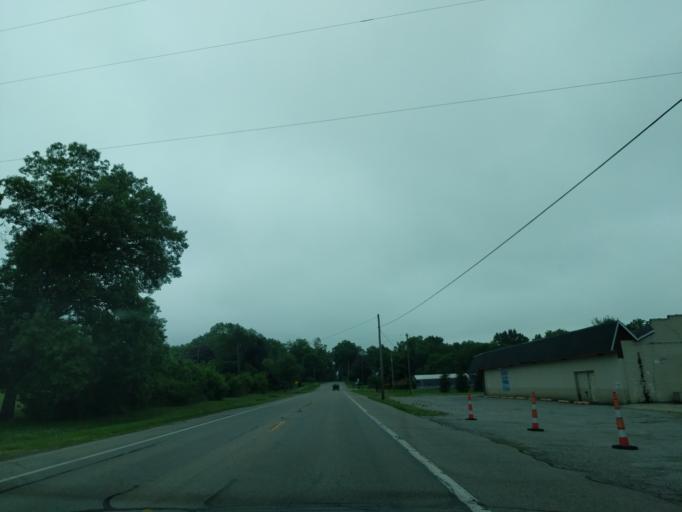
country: US
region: Michigan
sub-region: Hillsdale County
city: Litchfield
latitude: 42.0502
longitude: -84.7667
